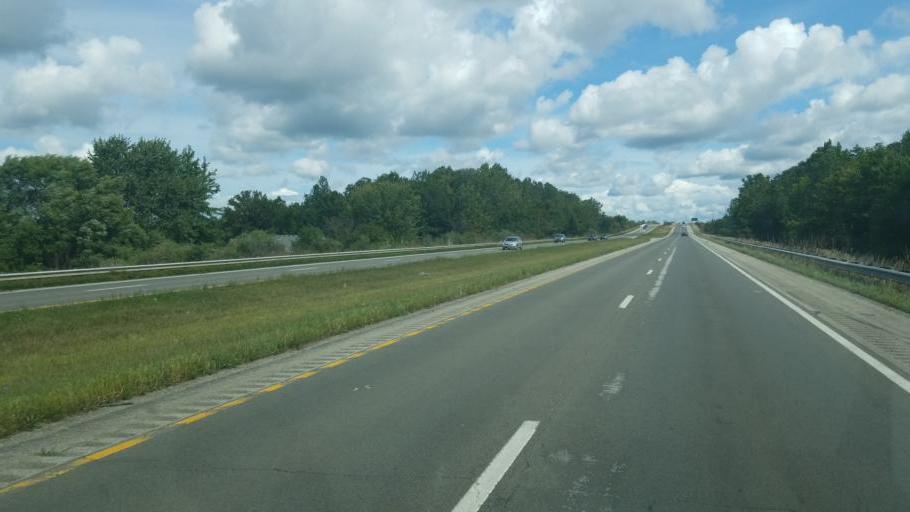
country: US
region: Ohio
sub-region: Lorain County
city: North Ridgeville
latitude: 41.3717
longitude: -81.9988
